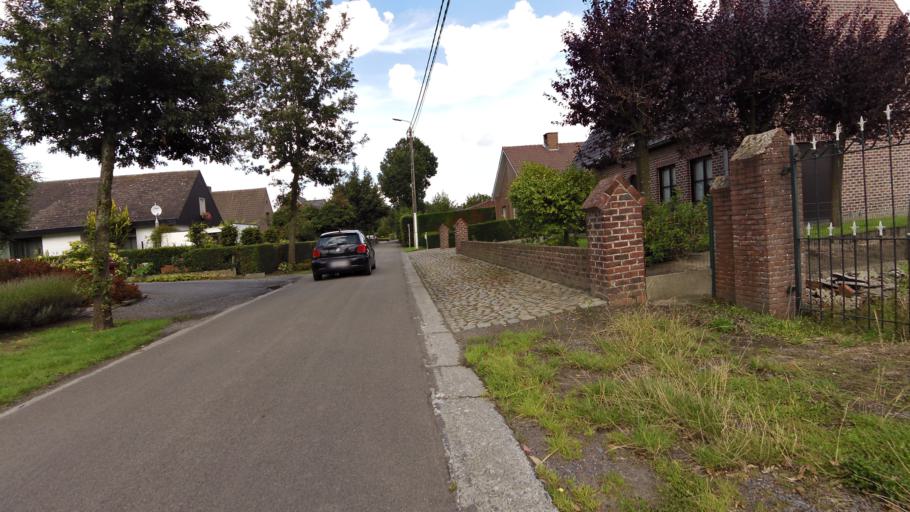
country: BE
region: Flanders
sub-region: Provincie West-Vlaanderen
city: Torhout
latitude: 51.0867
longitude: 3.0653
